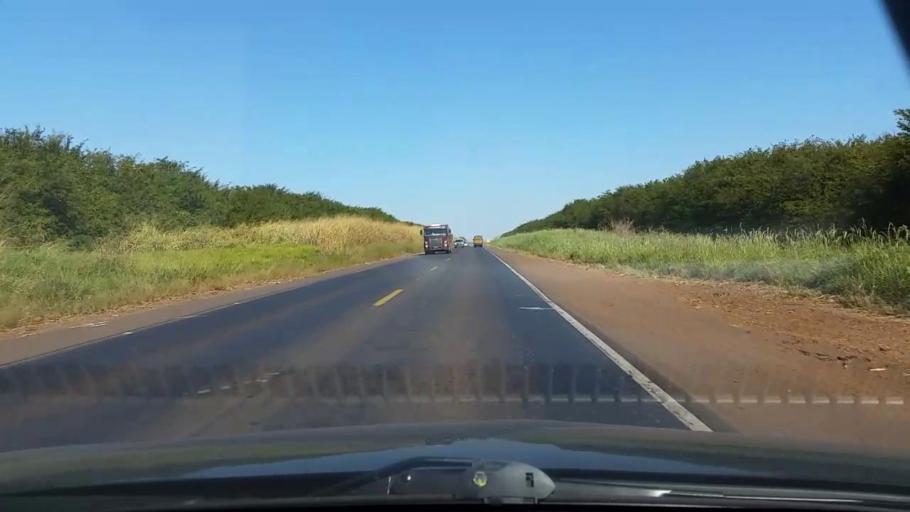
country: BR
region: Sao Paulo
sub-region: Igaracu Do Tiete
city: Igaracu do Tiete
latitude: -22.5548
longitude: -48.5608
